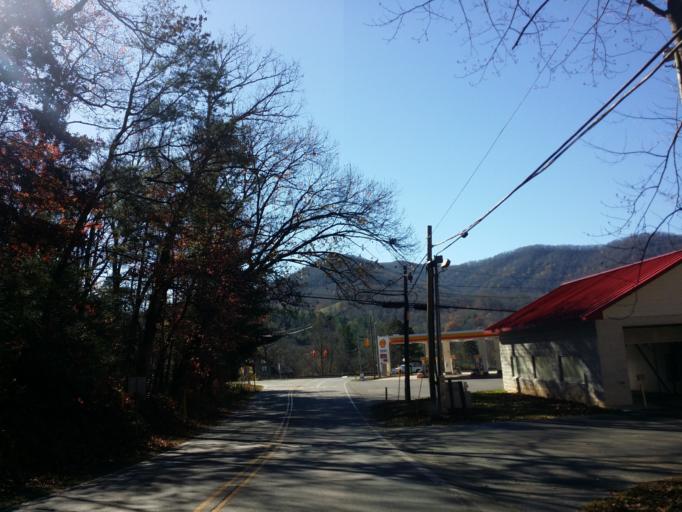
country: US
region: North Carolina
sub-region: Buncombe County
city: Swannanoa
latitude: 35.5939
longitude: -82.4359
